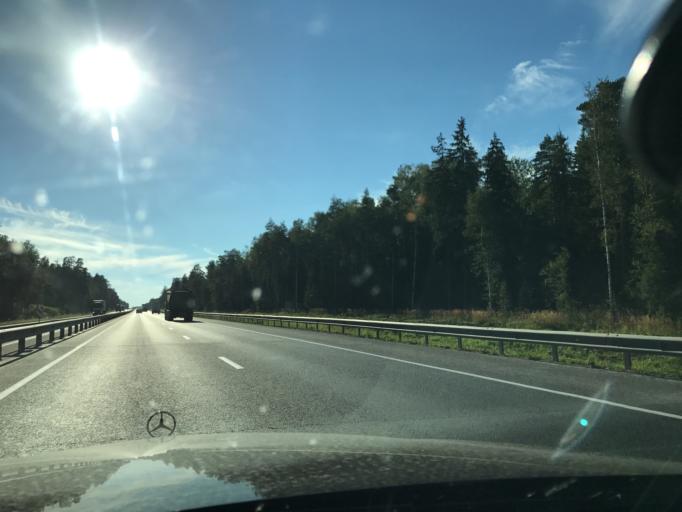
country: RU
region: Vladimir
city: Mstera
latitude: 56.2345
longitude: 41.8516
